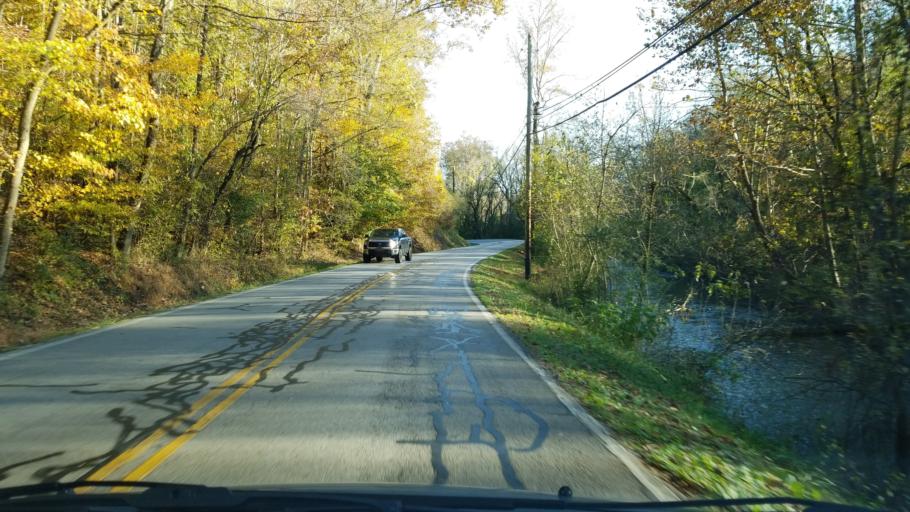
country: US
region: Tennessee
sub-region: Hamilton County
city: Falling Water
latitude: 35.1966
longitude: -85.2457
